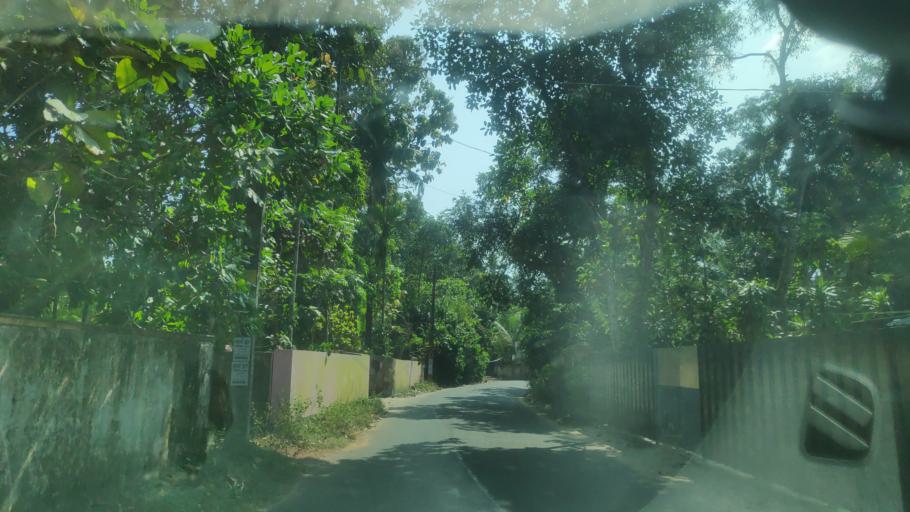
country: IN
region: Kerala
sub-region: Alappuzha
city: Vayalar
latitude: 9.6642
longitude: 76.3116
